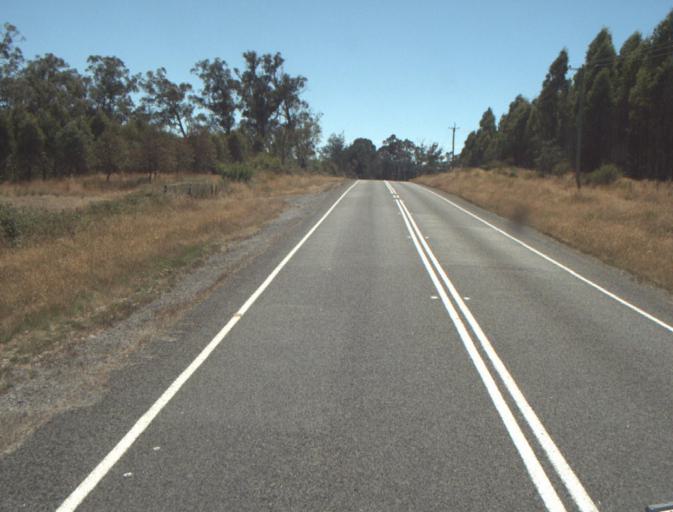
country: AU
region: Tasmania
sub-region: Launceston
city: Newstead
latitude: -41.3764
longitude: 147.3122
